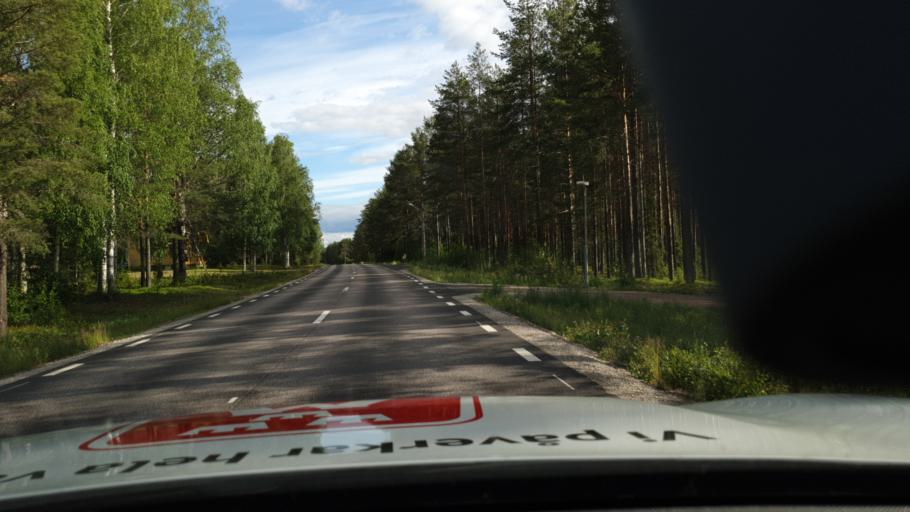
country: SE
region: Norrbotten
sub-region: Overkalix Kommun
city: OEverkalix
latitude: 66.4305
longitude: 22.7942
